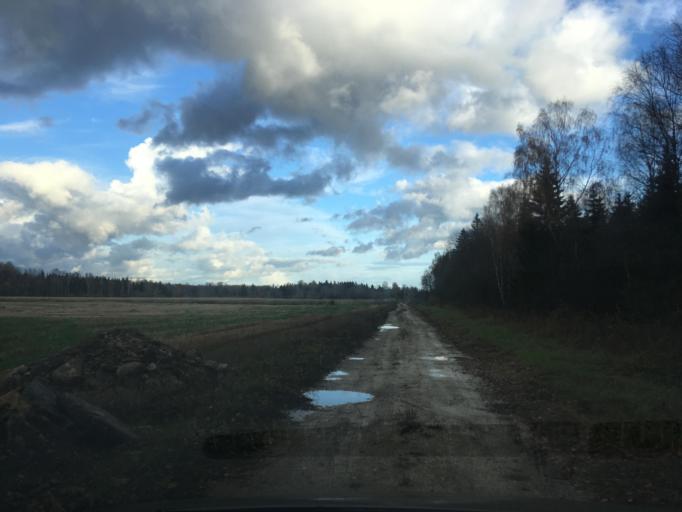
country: EE
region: Harju
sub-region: Raasiku vald
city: Arukula
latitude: 59.3587
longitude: 25.0961
